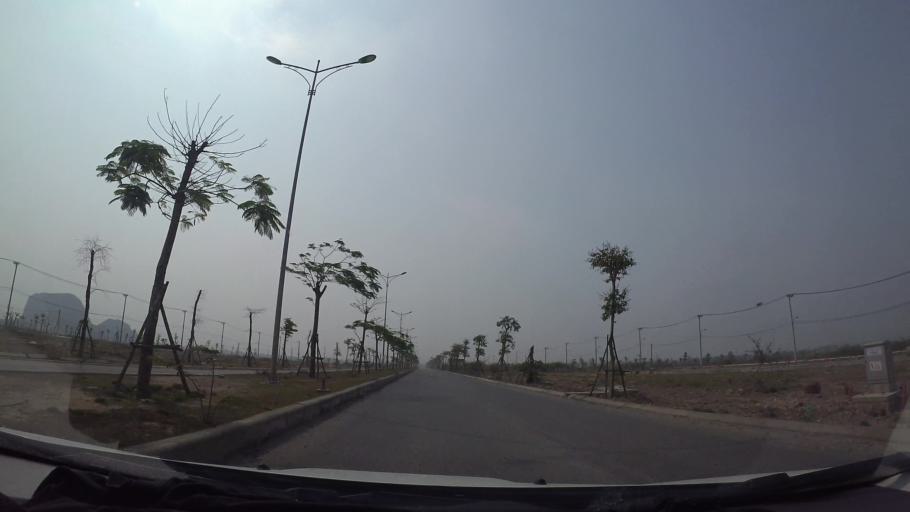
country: VN
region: Da Nang
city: Ngu Hanh Son
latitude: 16.0047
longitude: 108.2460
